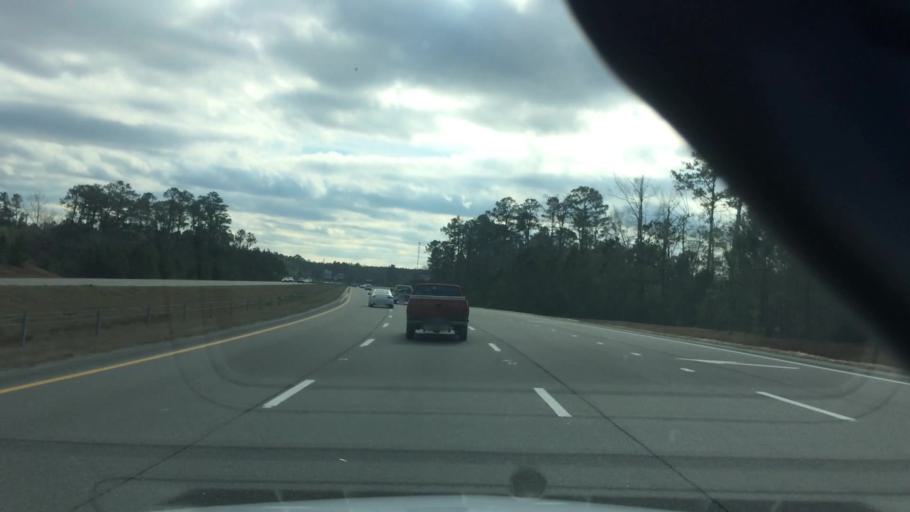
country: US
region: North Carolina
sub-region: Brunswick County
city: Leland
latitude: 34.1881
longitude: -78.0818
